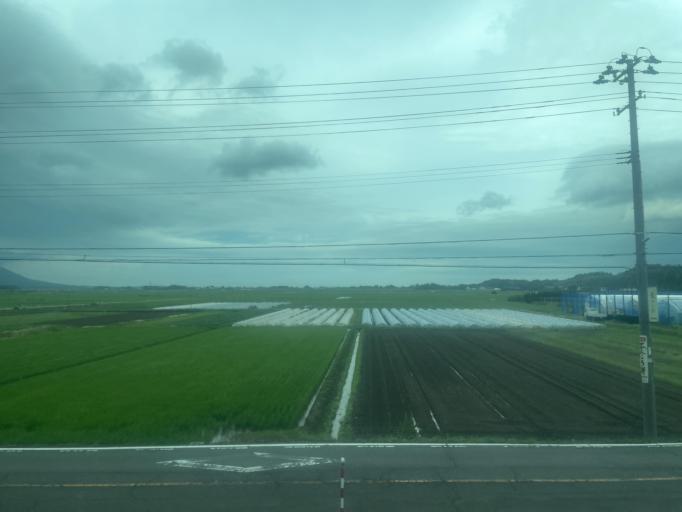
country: JP
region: Niigata
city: Yoshida-kasugacho
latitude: 37.6979
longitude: 138.8459
